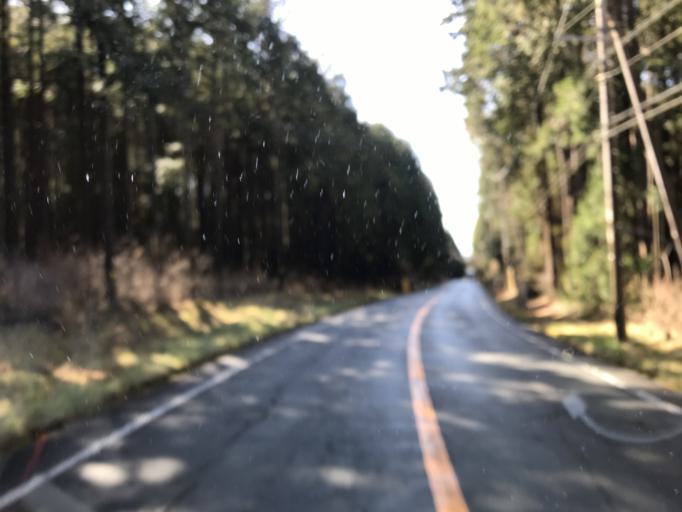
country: JP
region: Shizuoka
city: Fujinomiya
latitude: 35.2884
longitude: 138.6628
